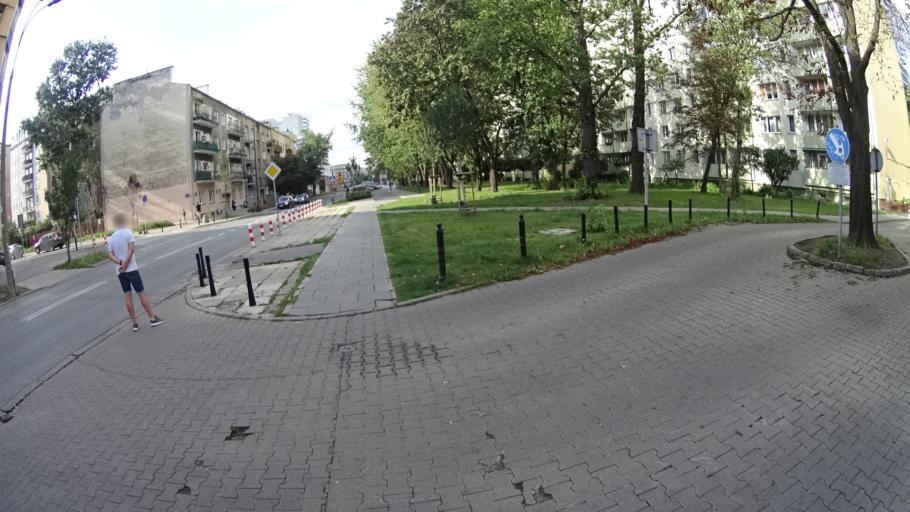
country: PL
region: Masovian Voivodeship
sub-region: Warszawa
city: Ochota
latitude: 52.2299
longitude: 20.9671
